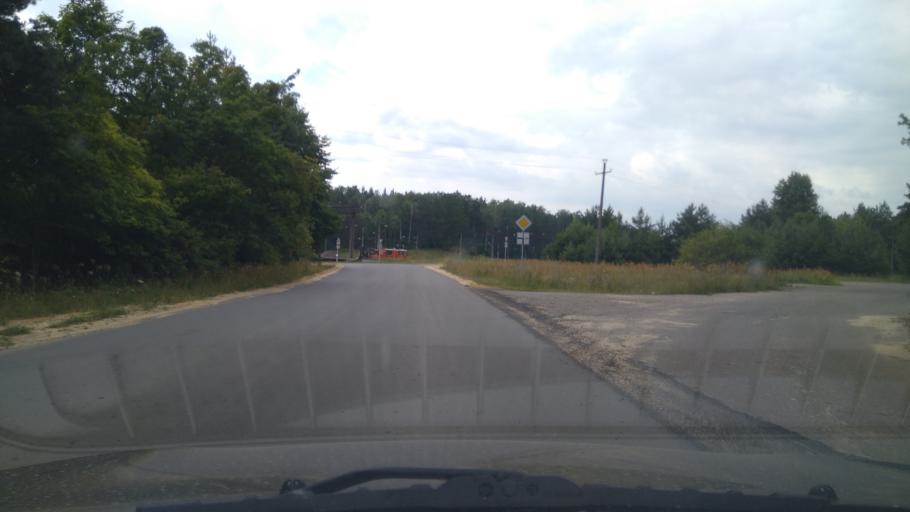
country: BY
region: Brest
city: Nyakhachava
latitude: 52.6056
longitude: 25.0855
